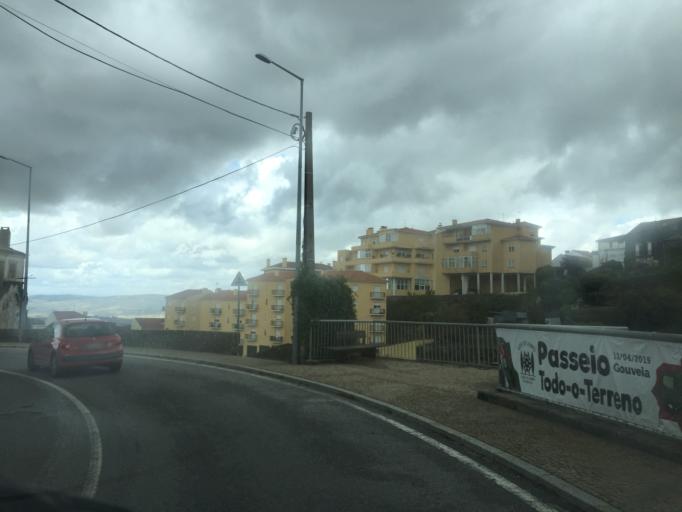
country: PT
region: Guarda
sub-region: Manteigas
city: Manteigas
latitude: 40.4932
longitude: -7.5956
